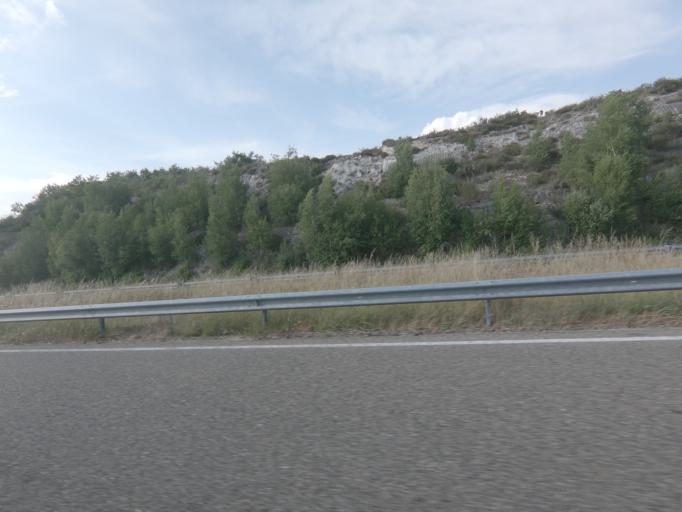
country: ES
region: Galicia
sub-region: Provincia de Ourense
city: Xinzo de Limia
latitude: 42.0651
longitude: -7.6981
